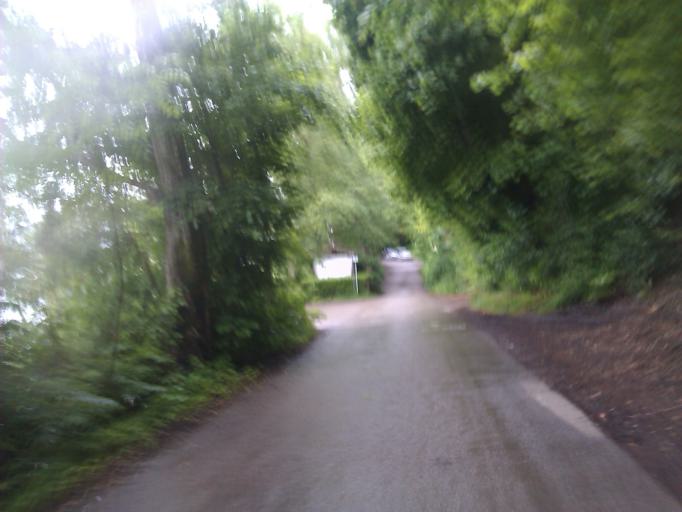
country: DE
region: Bavaria
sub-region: Swabia
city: Schwangau
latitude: 47.6099
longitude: 10.7192
